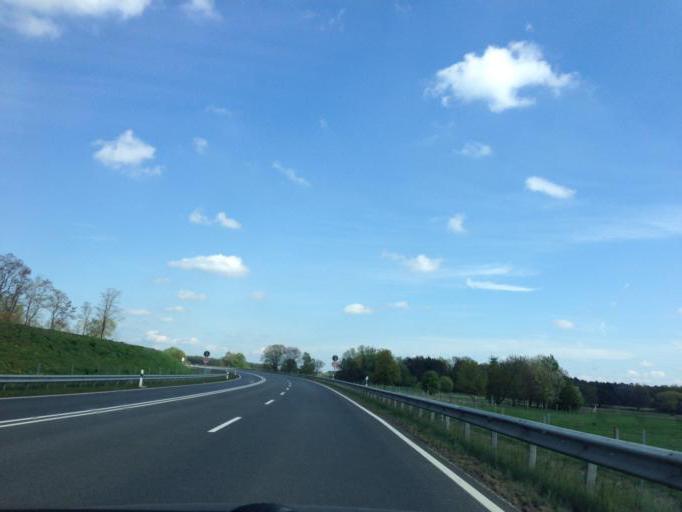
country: DE
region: Lower Saxony
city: Celle
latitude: 52.5933
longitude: 10.0796
